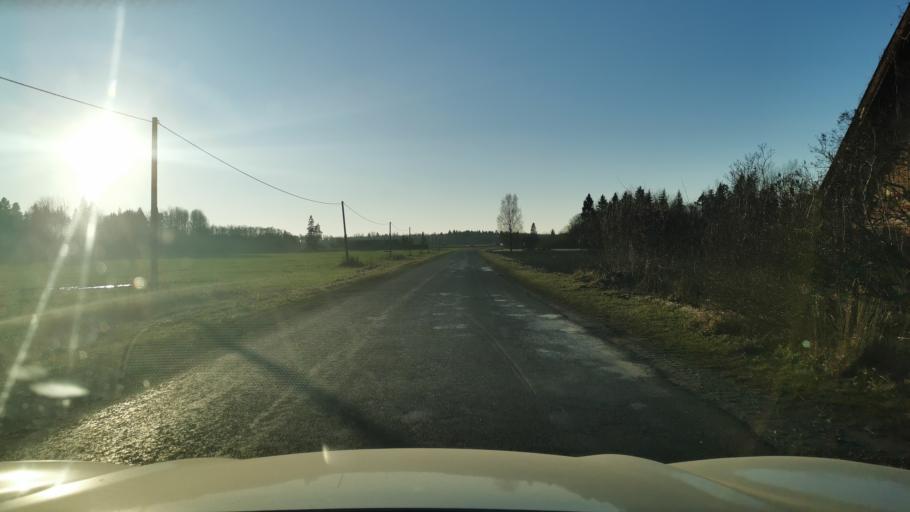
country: EE
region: Ida-Virumaa
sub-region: Kivioli linn
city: Kivioli
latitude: 59.3090
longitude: 26.9998
